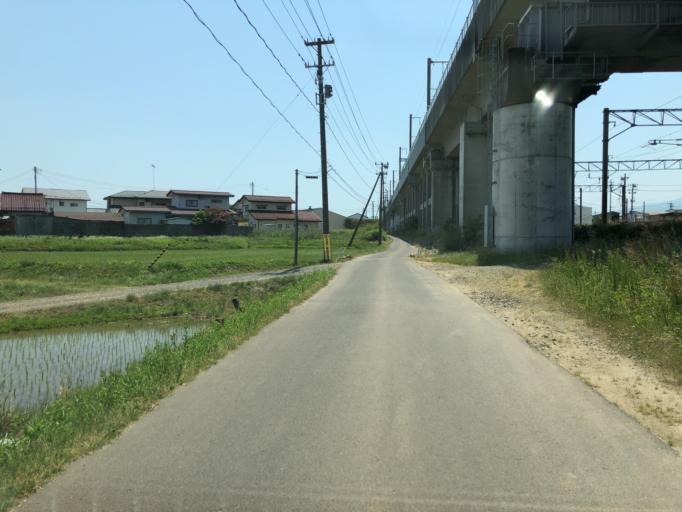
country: JP
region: Fukushima
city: Hobaramachi
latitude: 37.8275
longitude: 140.4961
